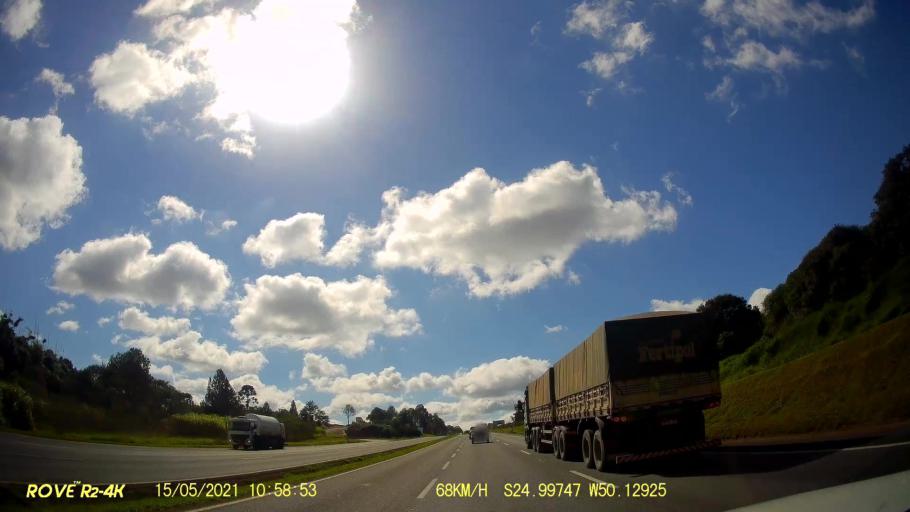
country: BR
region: Parana
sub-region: Carambei
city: Carambei
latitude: -24.9975
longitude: -50.1292
